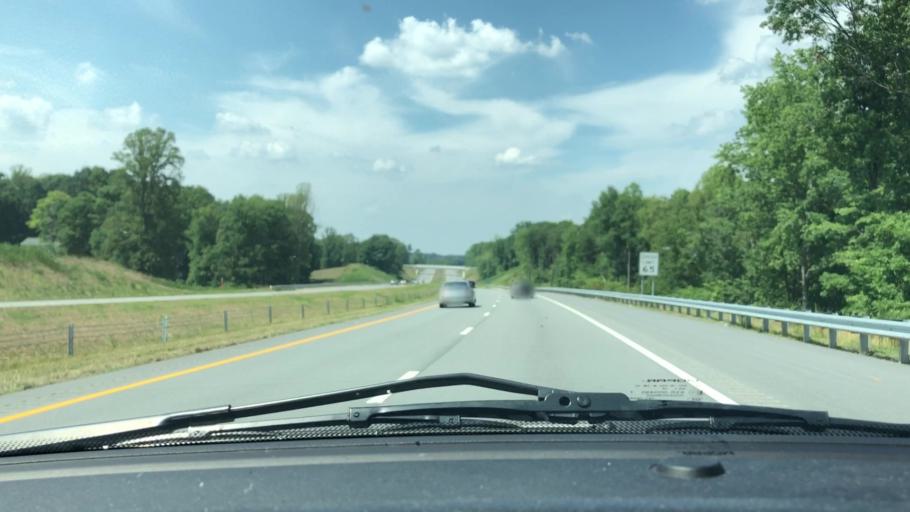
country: US
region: North Carolina
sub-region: Guilford County
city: Oak Ridge
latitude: 36.1450
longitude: -79.9585
